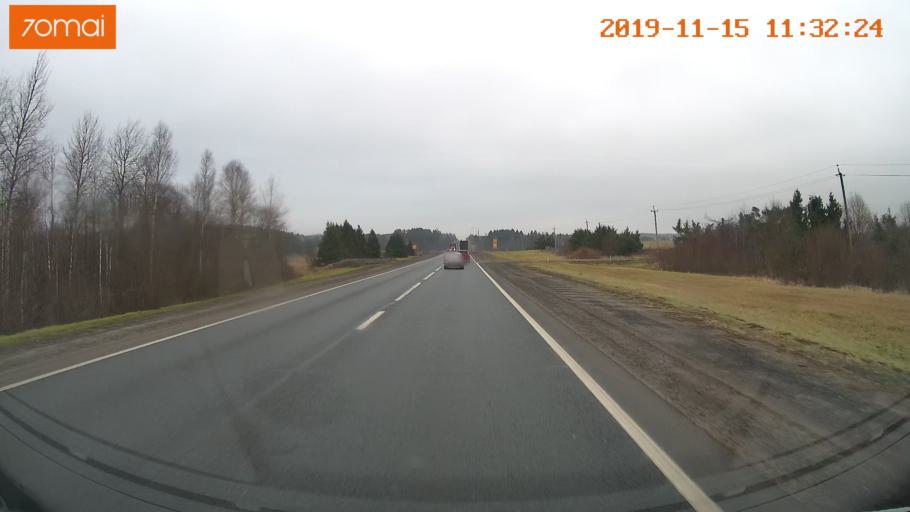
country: RU
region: Vologda
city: Molochnoye
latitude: 59.1854
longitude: 39.5732
